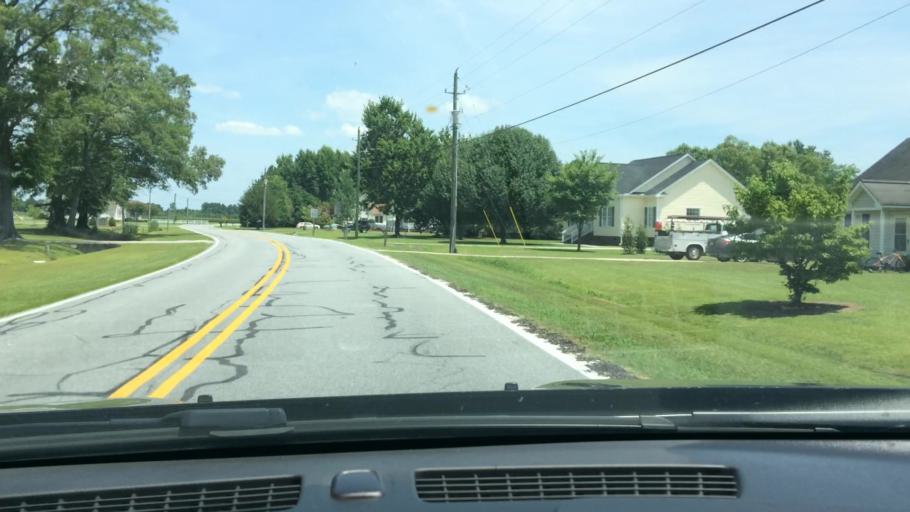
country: US
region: North Carolina
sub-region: Pitt County
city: Windsor
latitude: 35.5063
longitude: -77.3237
